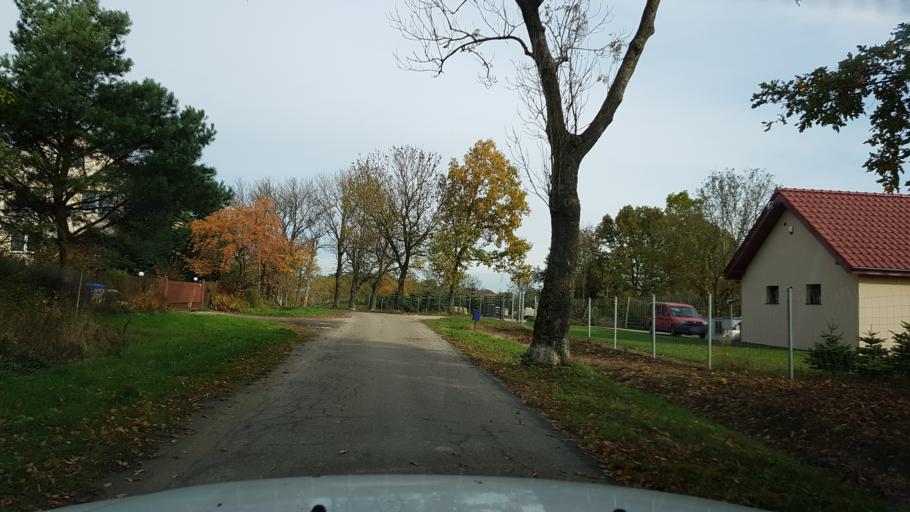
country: PL
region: West Pomeranian Voivodeship
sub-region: Powiat swidwinski
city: Polczyn-Zdroj
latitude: 53.7368
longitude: 16.0355
